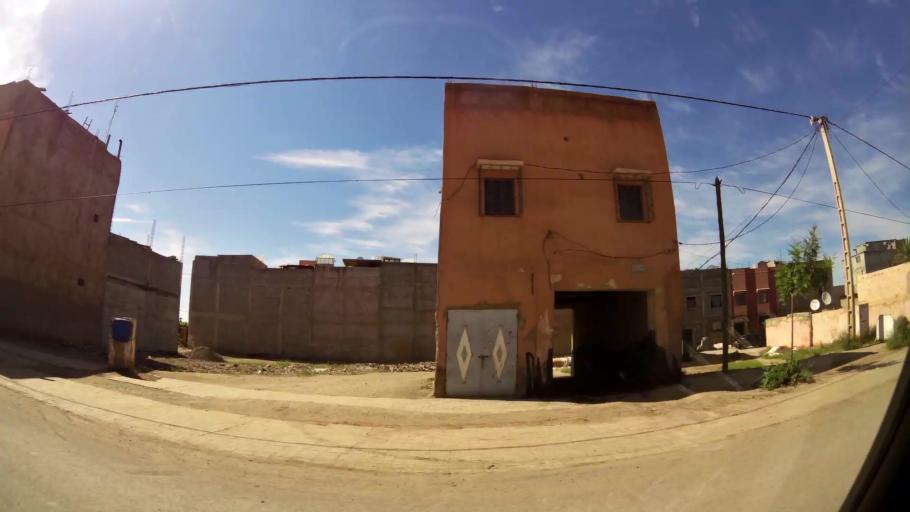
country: MA
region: Marrakech-Tensift-Al Haouz
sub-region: Marrakech
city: Marrakesh
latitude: 31.6295
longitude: -7.9588
